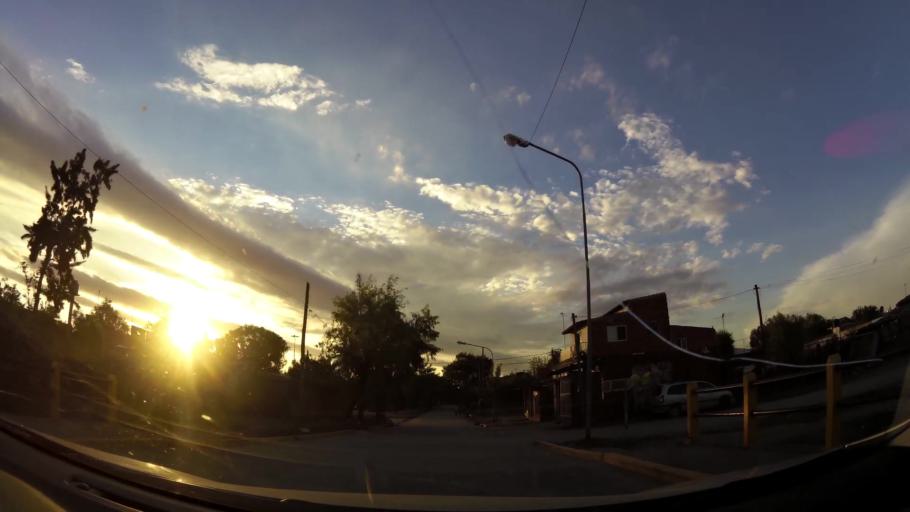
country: AR
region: Buenos Aires
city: Santa Catalina - Dique Lujan
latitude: -34.4402
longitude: -58.6628
